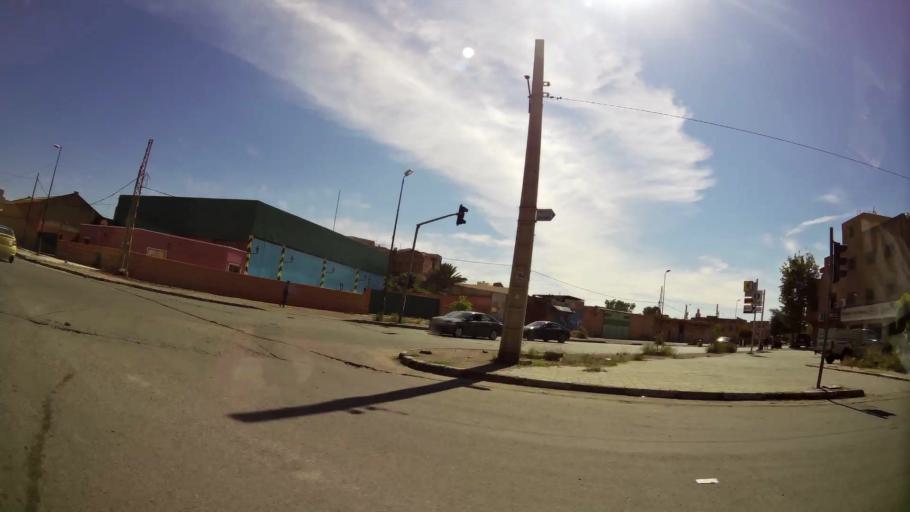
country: MA
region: Marrakech-Tensift-Al Haouz
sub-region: Marrakech
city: Marrakesh
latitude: 31.6345
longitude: -8.0409
